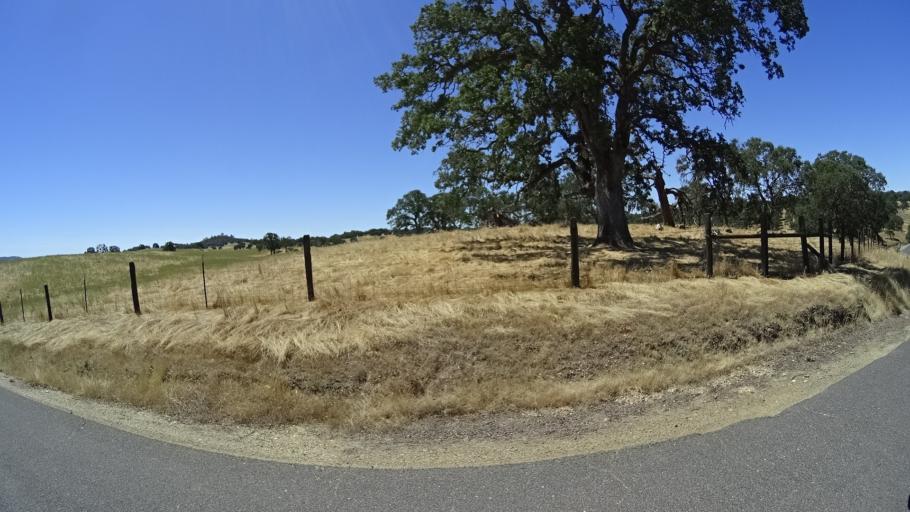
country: US
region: California
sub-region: Calaveras County
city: Copperopolis
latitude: 38.0286
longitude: -120.7199
